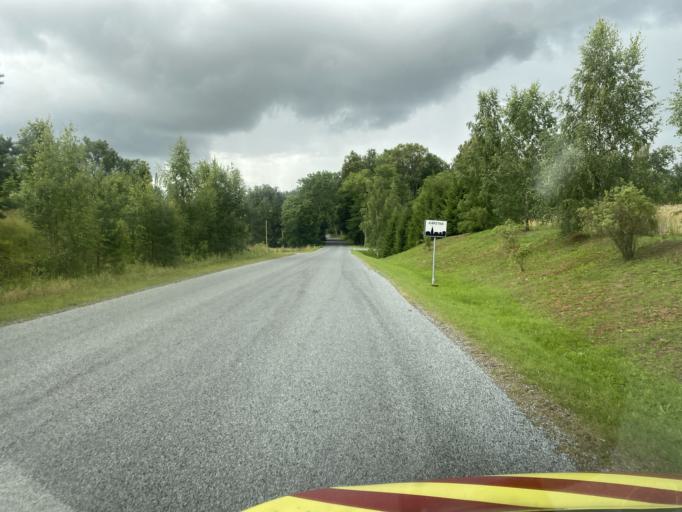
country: EE
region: Valgamaa
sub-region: Torva linn
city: Torva
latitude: 58.1491
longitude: 25.8047
